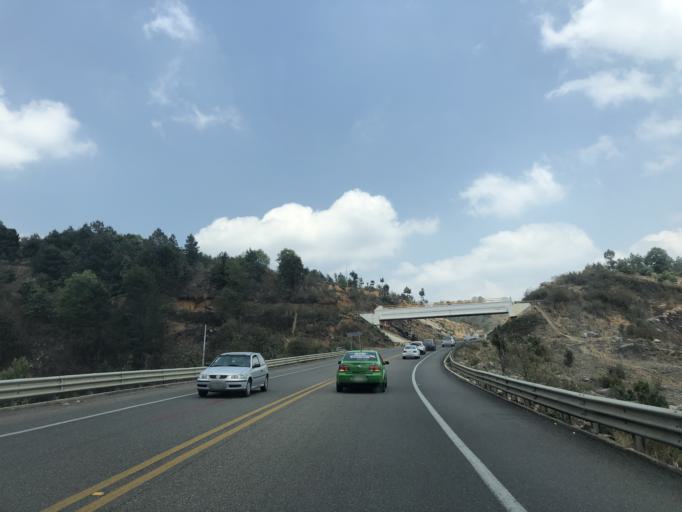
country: MX
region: Chiapas
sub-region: Zinacantan
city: Nachig
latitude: 16.6896
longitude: -92.7280
